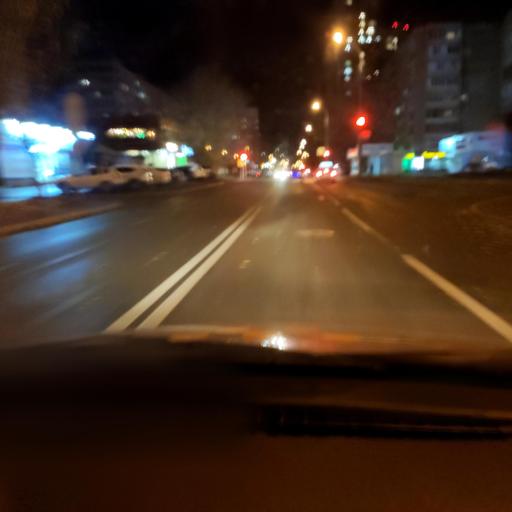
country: RU
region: Bashkortostan
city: Ufa
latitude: 54.7667
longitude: 56.0617
